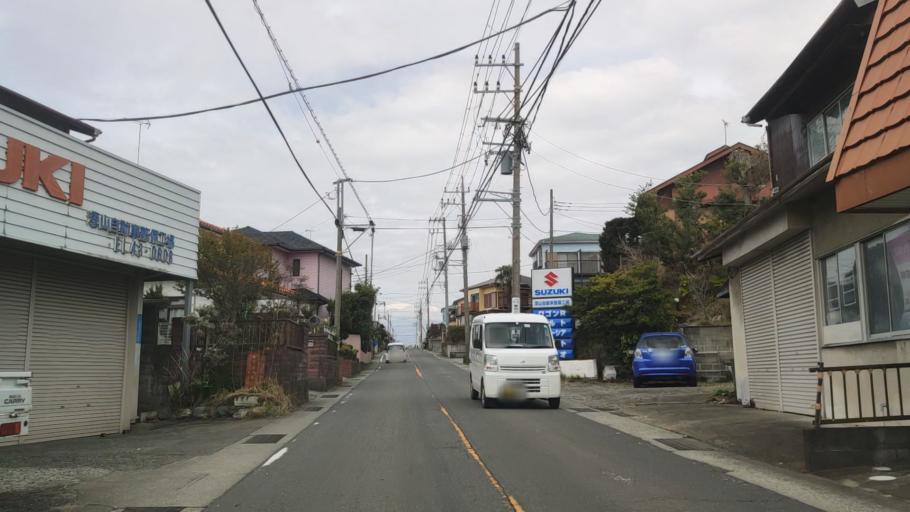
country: JP
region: Kanagawa
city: Ninomiya
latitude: 35.2934
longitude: 139.2338
